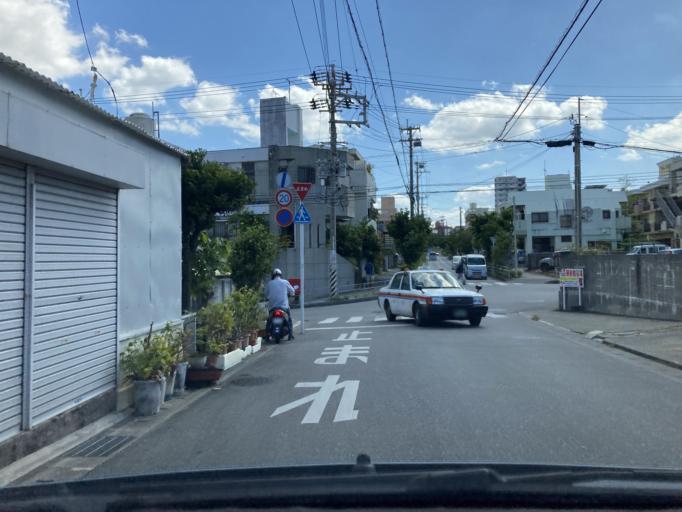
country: JP
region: Okinawa
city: Naha-shi
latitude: 26.2030
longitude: 127.6898
